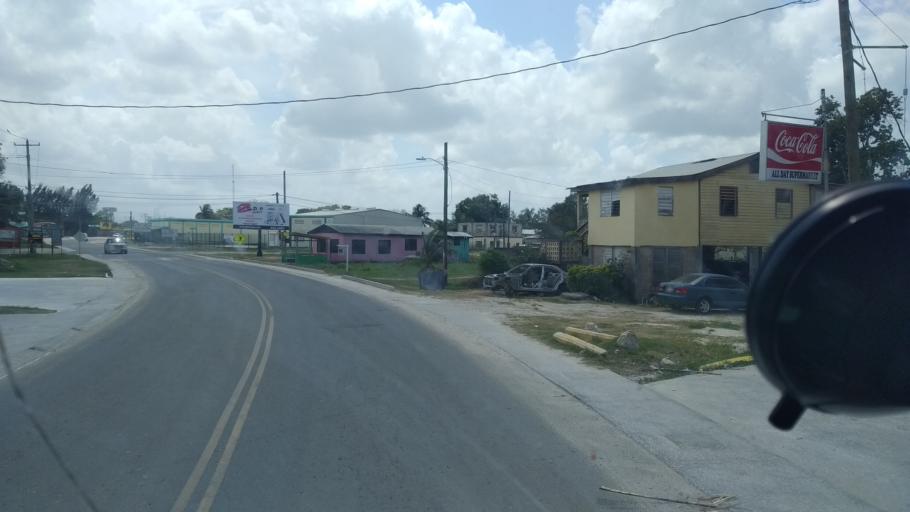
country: BZ
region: Orange Walk
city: Orange Walk
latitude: 18.0676
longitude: -88.5711
